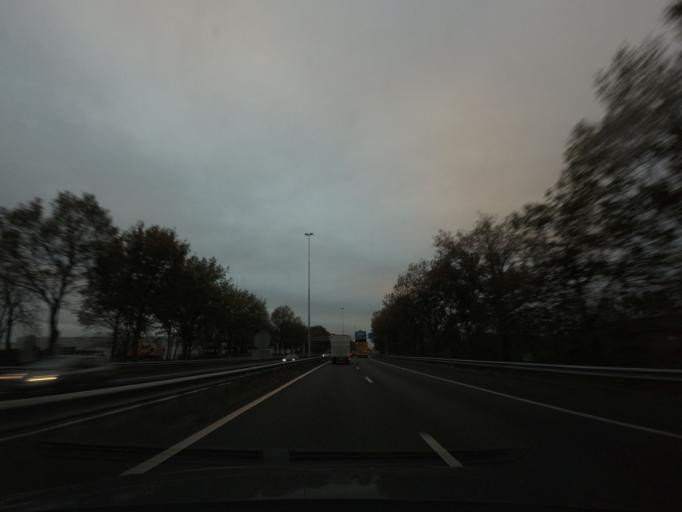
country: NL
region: North Brabant
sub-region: Gemeente Oosterhout
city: Oosterhout
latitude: 51.6360
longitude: 4.8812
